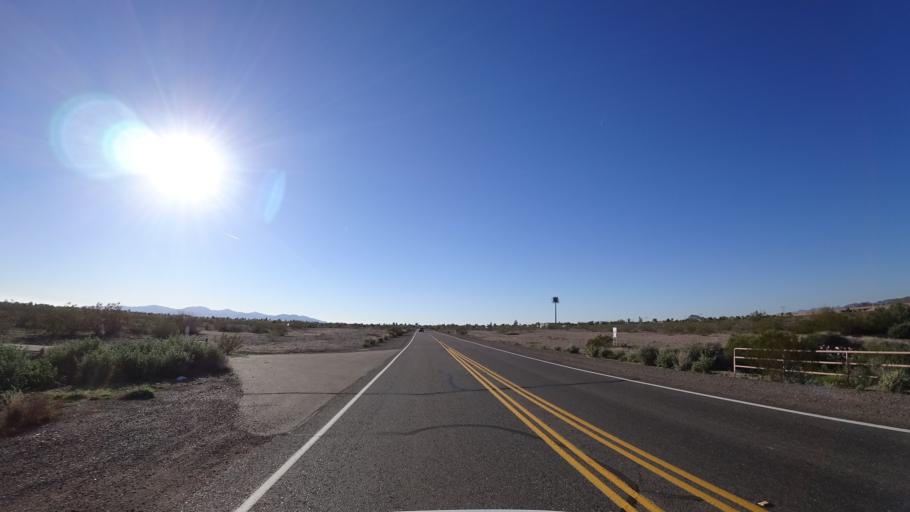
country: US
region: Arizona
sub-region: Maricopa County
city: Sun City West
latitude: 33.6893
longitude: -112.3283
